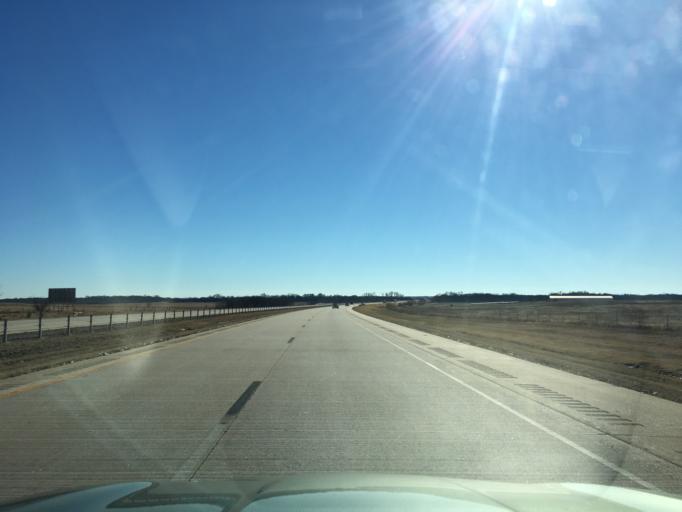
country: US
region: Oklahoma
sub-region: Kay County
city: Tonkawa
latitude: 36.4886
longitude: -97.3288
